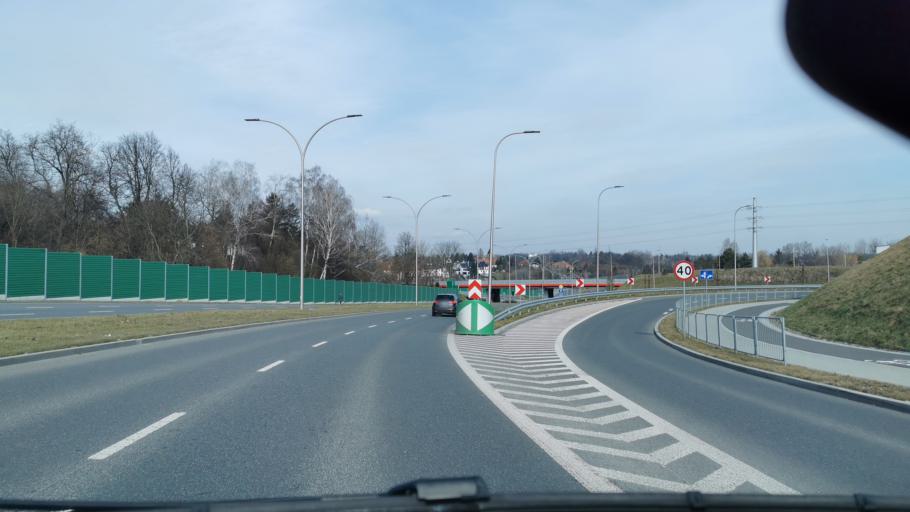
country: PL
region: Lublin Voivodeship
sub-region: Powiat lubelski
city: Lublin
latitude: 51.2498
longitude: 22.5048
